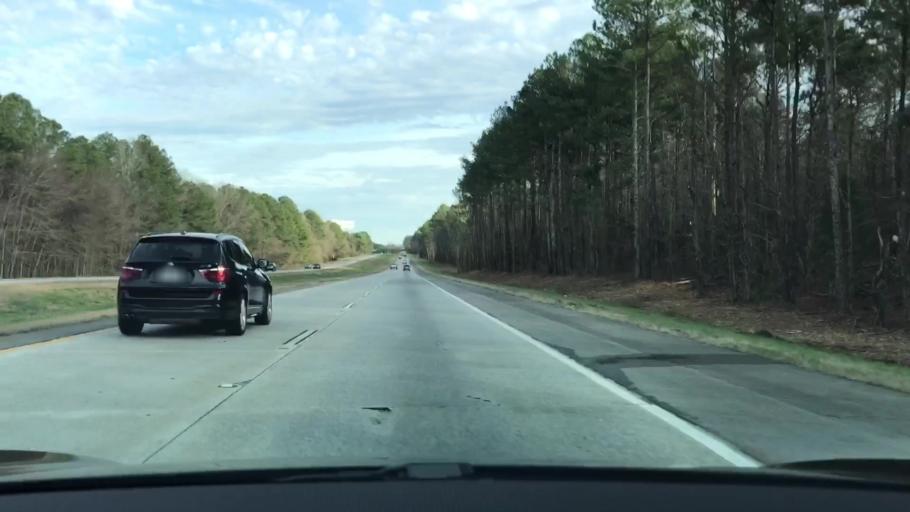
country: US
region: Georgia
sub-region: Taliaferro County
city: Crawfordville
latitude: 33.5295
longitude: -82.9702
